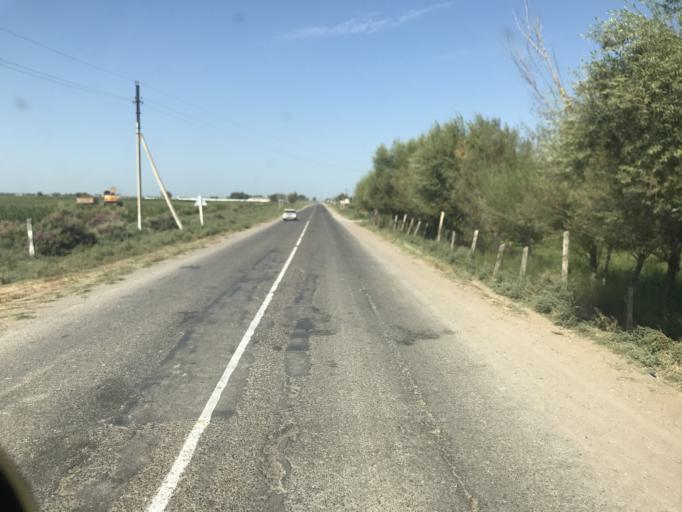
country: KZ
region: Ongtustik Qazaqstan
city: Myrzakent
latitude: 40.6855
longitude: 68.5686
